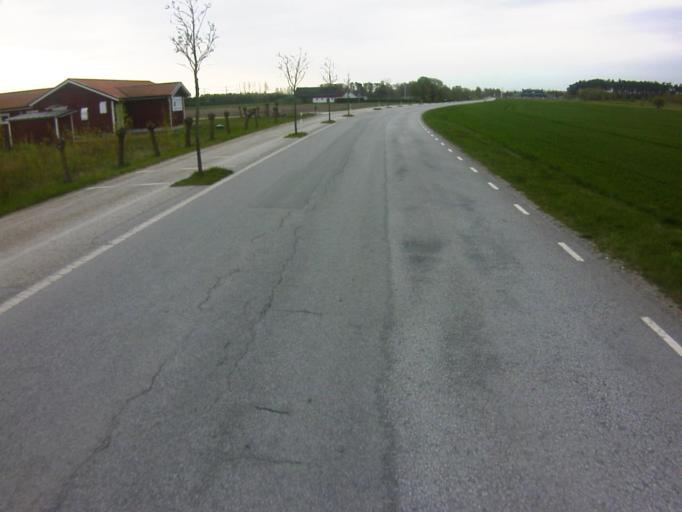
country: SE
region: Skane
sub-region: Kavlinge Kommun
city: Loddekopinge
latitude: 55.7739
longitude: 13.0105
